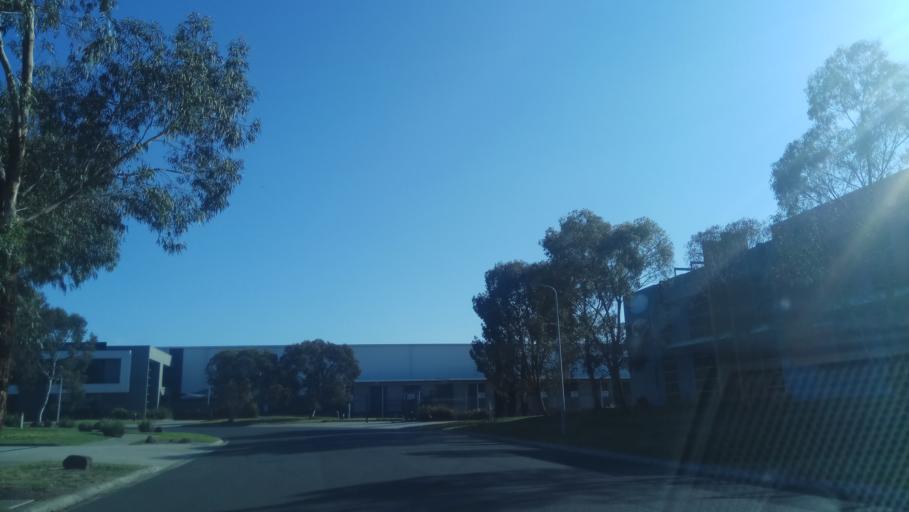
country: AU
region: Victoria
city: Heatherton
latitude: -37.9483
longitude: 145.0849
